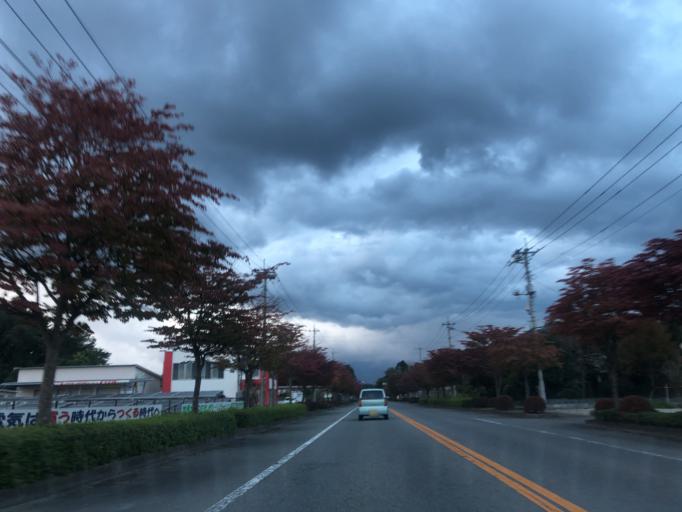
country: JP
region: Tochigi
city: Kuroiso
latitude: 36.9491
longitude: 140.0054
